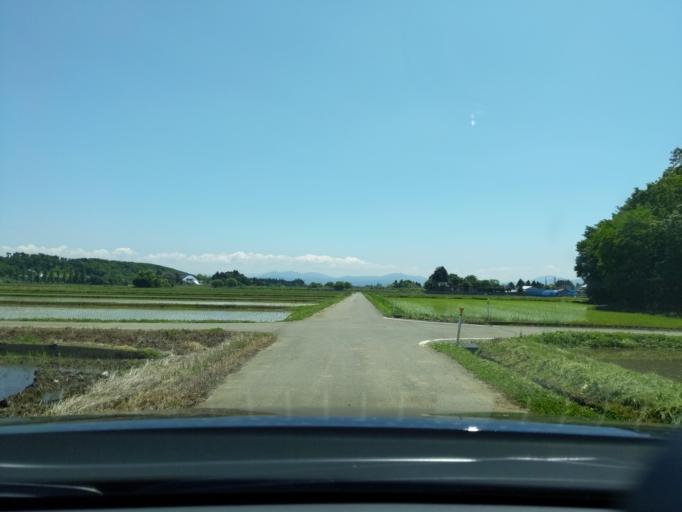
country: JP
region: Fukushima
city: Koriyama
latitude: 37.3936
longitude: 140.2932
